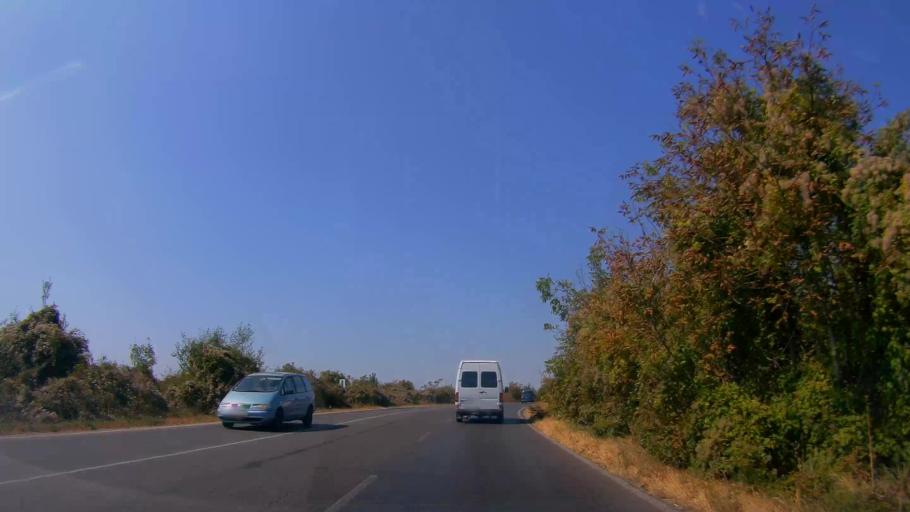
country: BG
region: Razgrad
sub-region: Obshtina Tsar Kaloyan
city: Tsar Kaloyan
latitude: 43.6277
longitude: 26.2075
